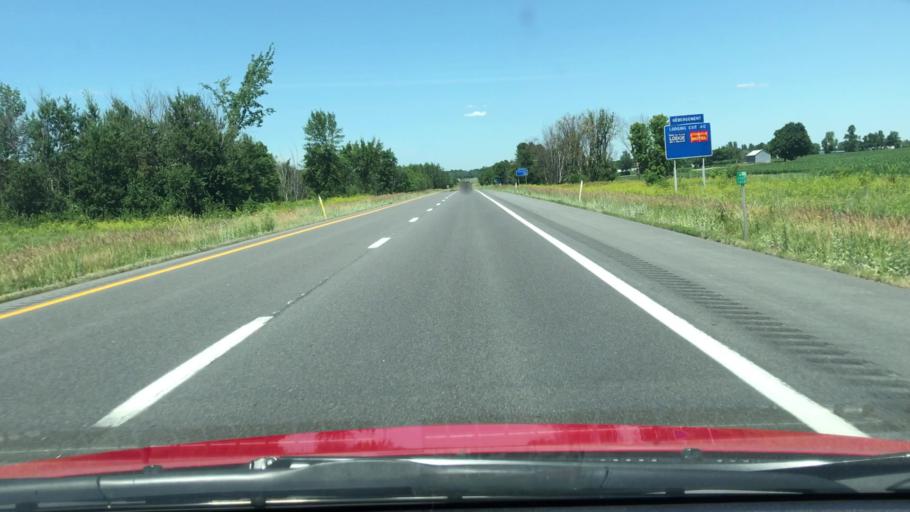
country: US
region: New York
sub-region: Clinton County
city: Cumberland Head
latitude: 44.7692
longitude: -73.4331
